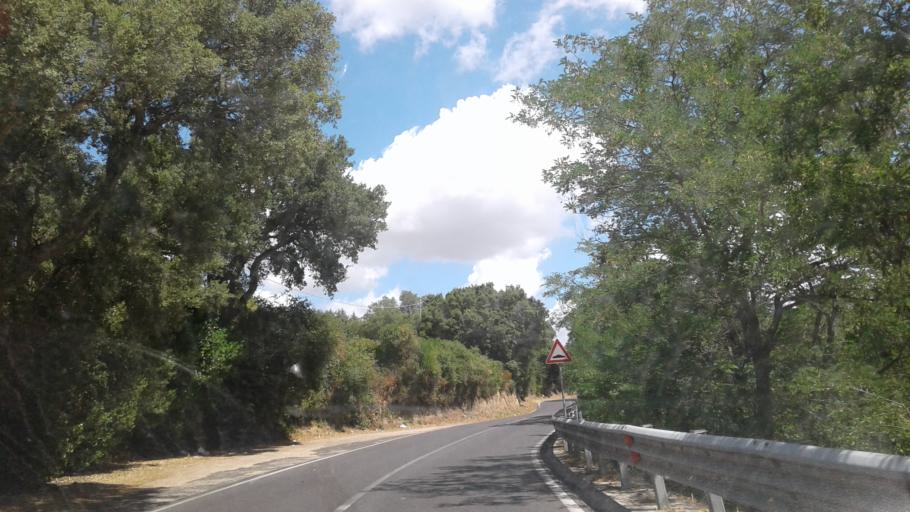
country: IT
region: Sardinia
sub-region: Provincia di Olbia-Tempio
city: Luras
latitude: 40.9192
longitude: 9.1746
